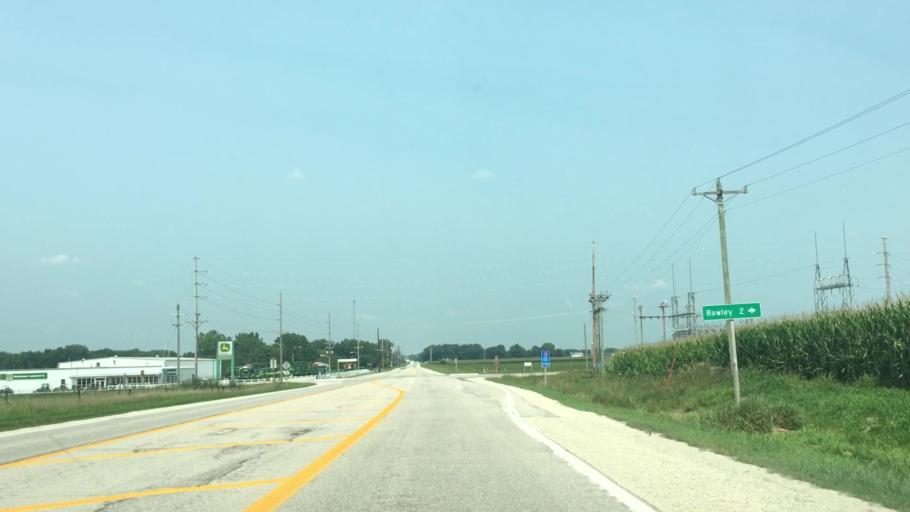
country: US
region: Iowa
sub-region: Buchanan County
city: Independence
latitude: 42.3694
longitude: -91.8893
